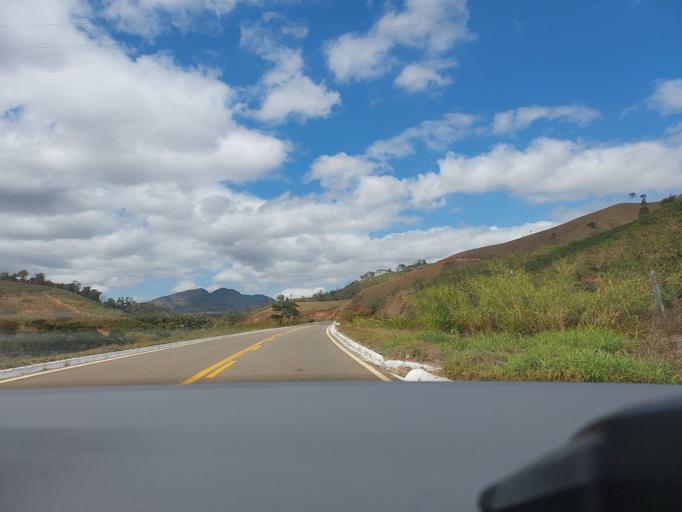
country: BR
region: Minas Gerais
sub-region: Visconde Do Rio Branco
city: Visconde do Rio Branco
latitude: -20.9313
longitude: -42.6332
